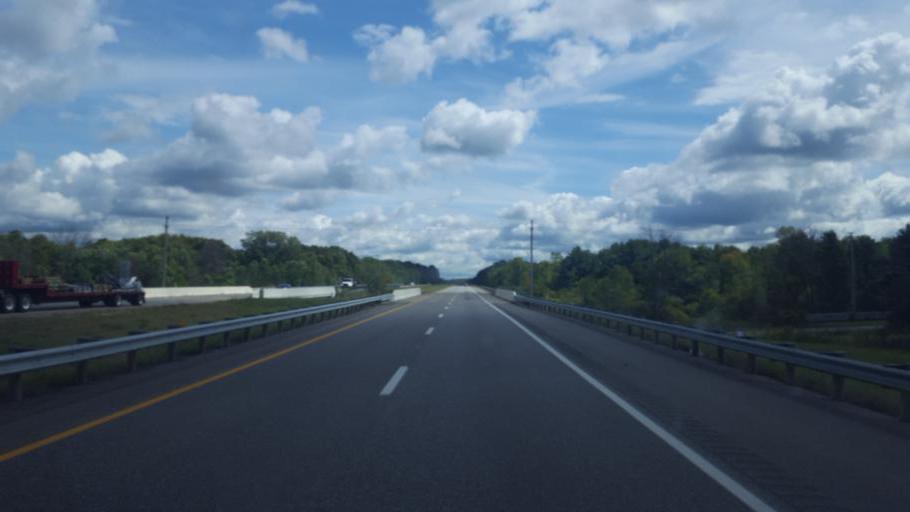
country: US
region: Ohio
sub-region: Geauga County
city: Bainbridge
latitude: 41.3838
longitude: -81.3096
